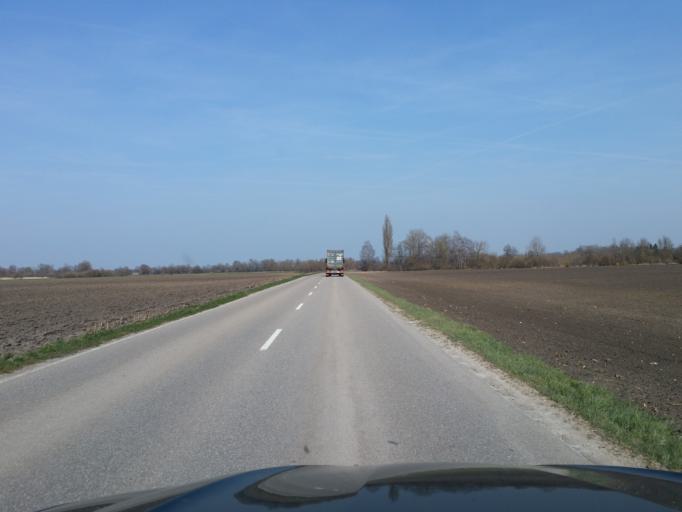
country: DE
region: Bavaria
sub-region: Upper Bavaria
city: Eitting
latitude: 48.3941
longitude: 11.8989
